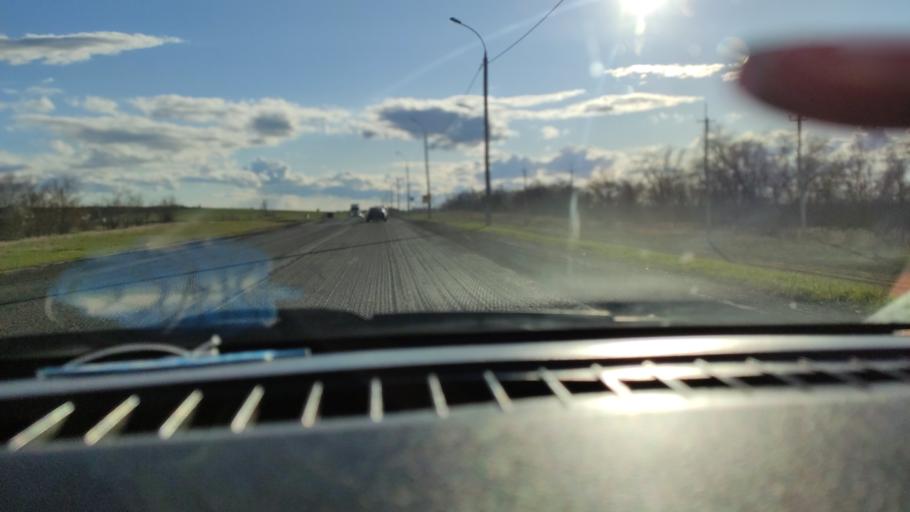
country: RU
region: Saratov
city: Shumeyka
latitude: 51.7906
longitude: 46.1520
